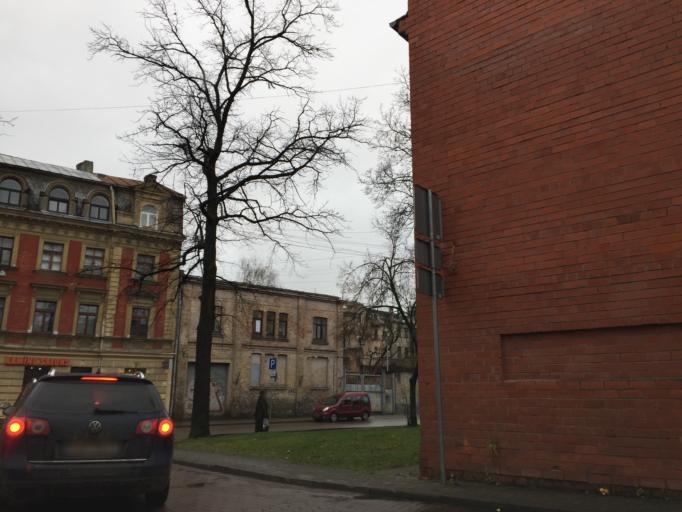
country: LV
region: Riga
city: Riga
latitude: 56.9662
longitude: 24.1419
